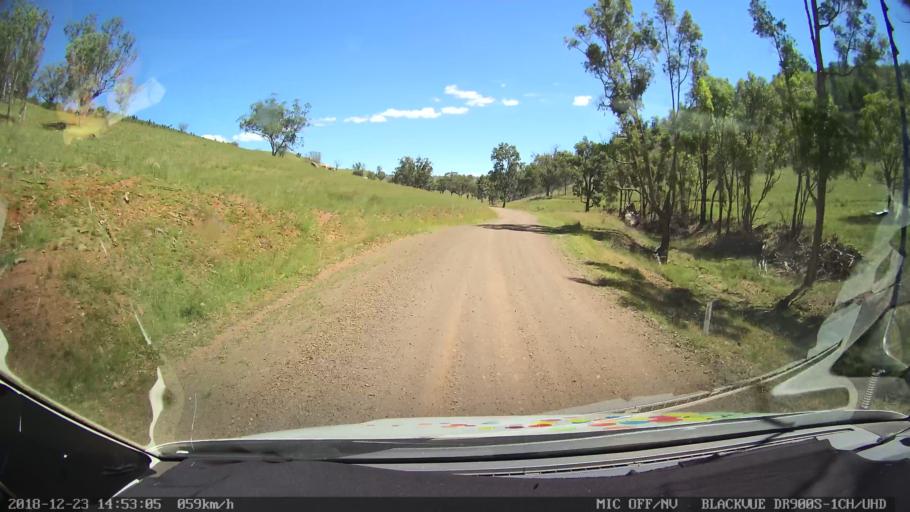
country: AU
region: New South Wales
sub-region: Tamworth Municipality
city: Manilla
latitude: -30.6888
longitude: 150.8521
